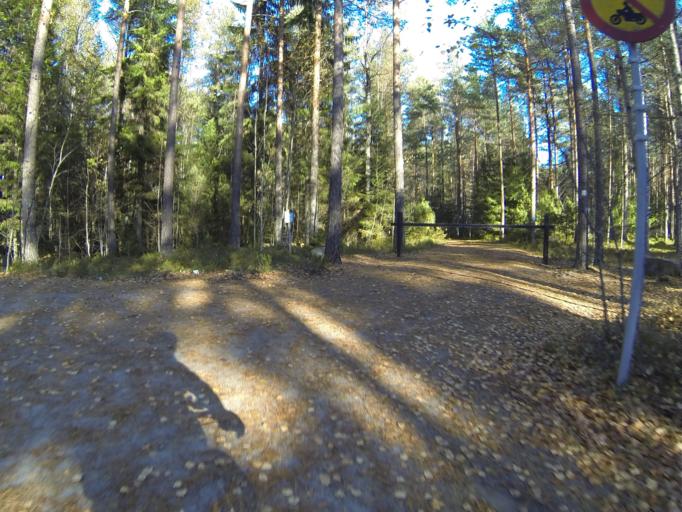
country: FI
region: Varsinais-Suomi
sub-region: Salo
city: Saerkisalo
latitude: 60.2096
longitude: 22.9250
